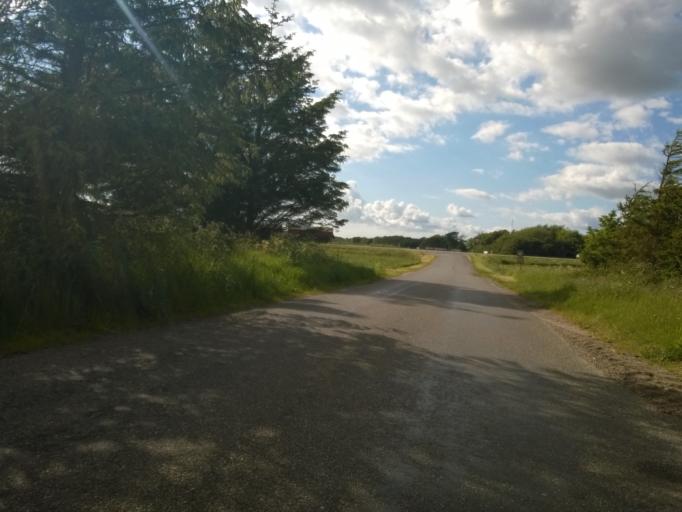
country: DK
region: Central Jutland
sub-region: Holstebro Kommune
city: Vinderup
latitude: 56.5138
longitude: 8.8090
